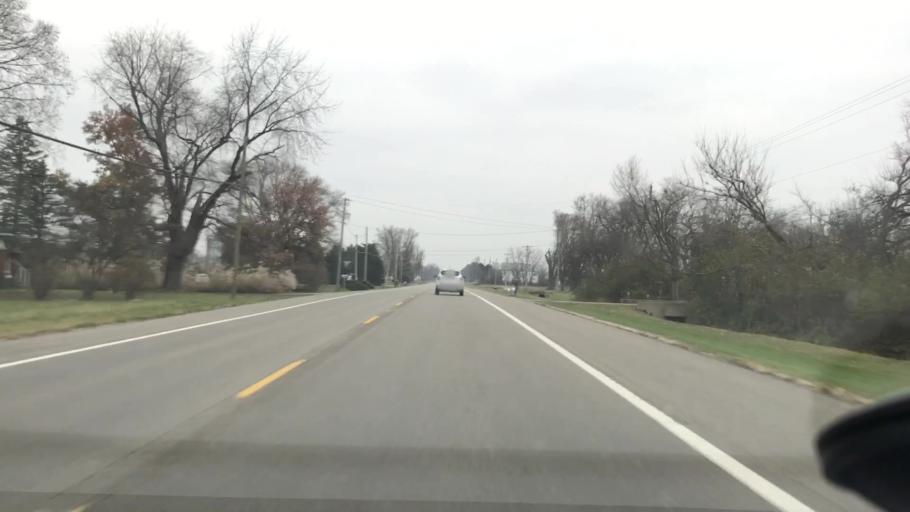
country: US
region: Ohio
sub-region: Greene County
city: Yellow Springs
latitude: 39.8530
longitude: -83.8555
